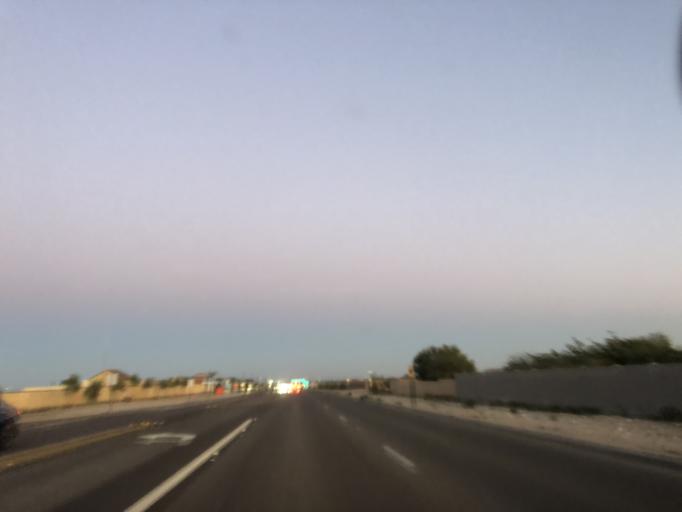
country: US
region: Arizona
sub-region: Maricopa County
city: Citrus Park
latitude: 33.4937
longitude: -112.4861
